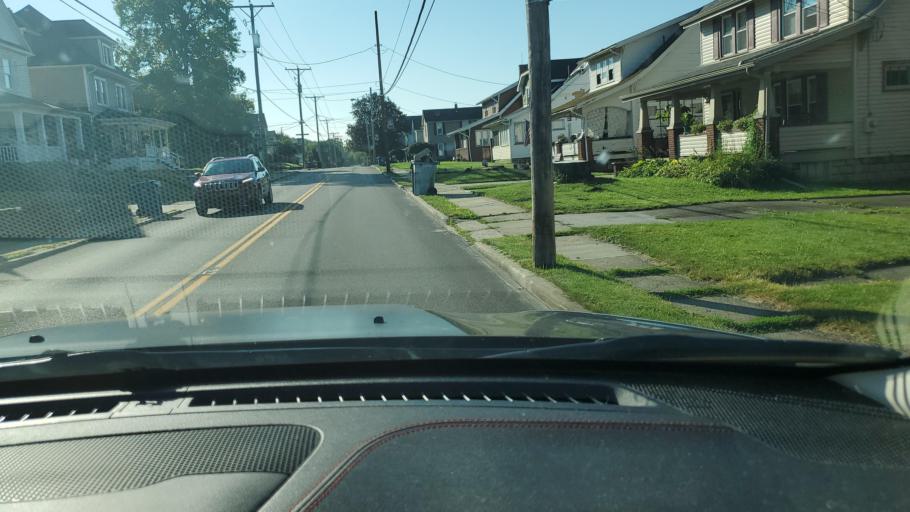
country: US
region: Ohio
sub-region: Mahoning County
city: Lowellville
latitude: 41.0405
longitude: -80.5406
